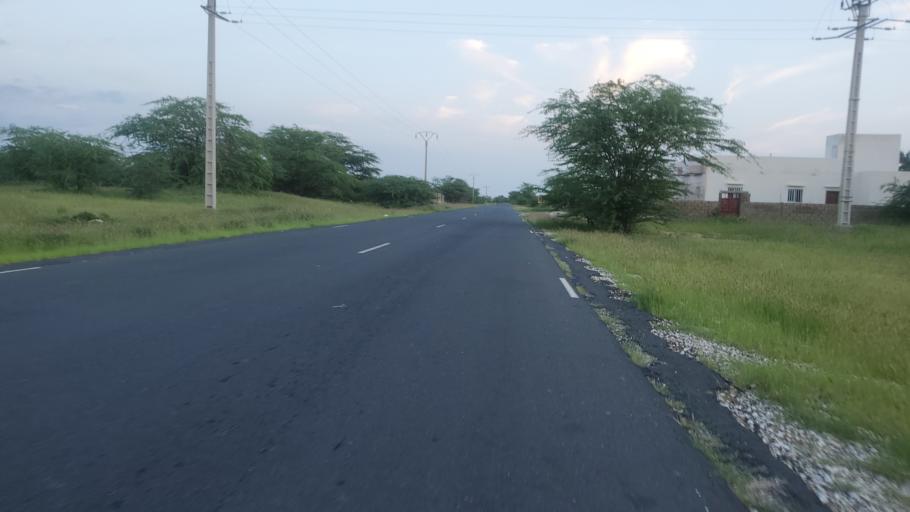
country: SN
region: Saint-Louis
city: Saint-Louis
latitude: 16.1073
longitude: -16.4122
